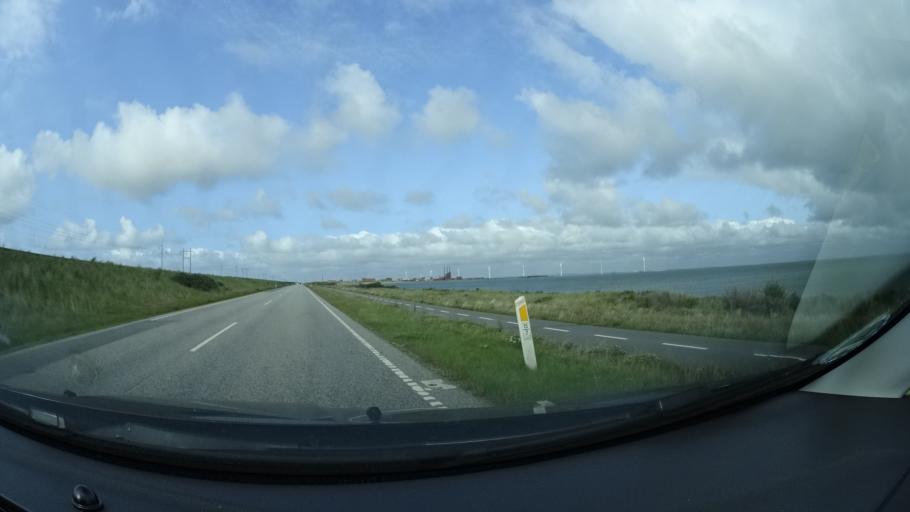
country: DK
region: Central Jutland
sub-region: Lemvig Kommune
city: Harboore
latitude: 56.6416
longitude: 8.1886
